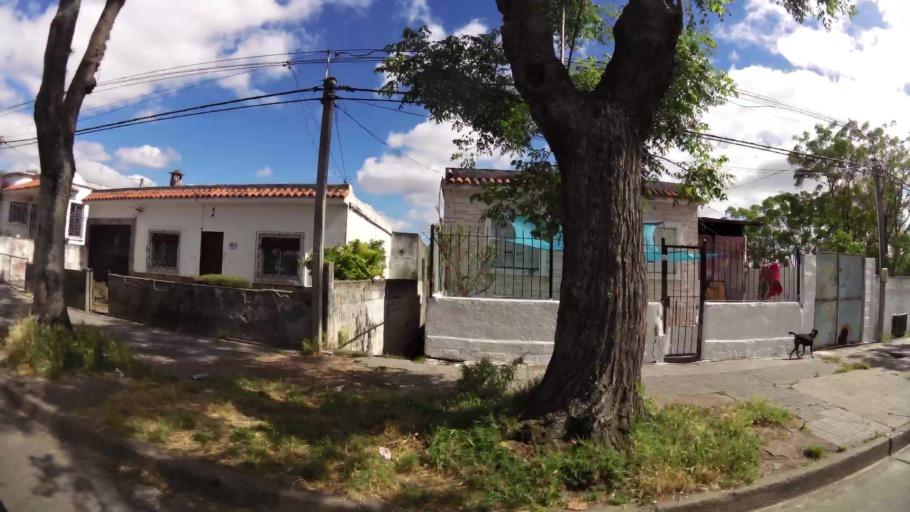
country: UY
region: Canelones
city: Paso de Carrasco
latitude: -34.8702
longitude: -56.1202
